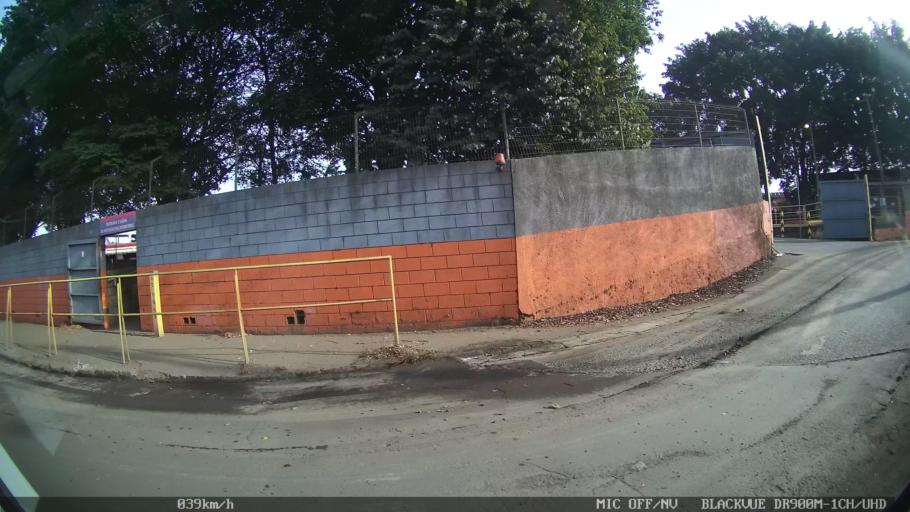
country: BR
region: Sao Paulo
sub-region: Piracicaba
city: Piracicaba
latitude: -22.6992
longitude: -47.6548
